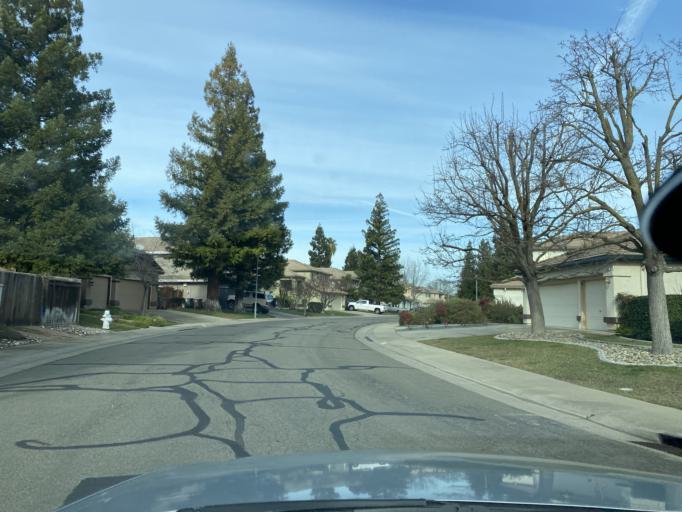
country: US
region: California
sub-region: Sacramento County
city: Elk Grove
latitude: 38.4324
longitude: -121.3804
